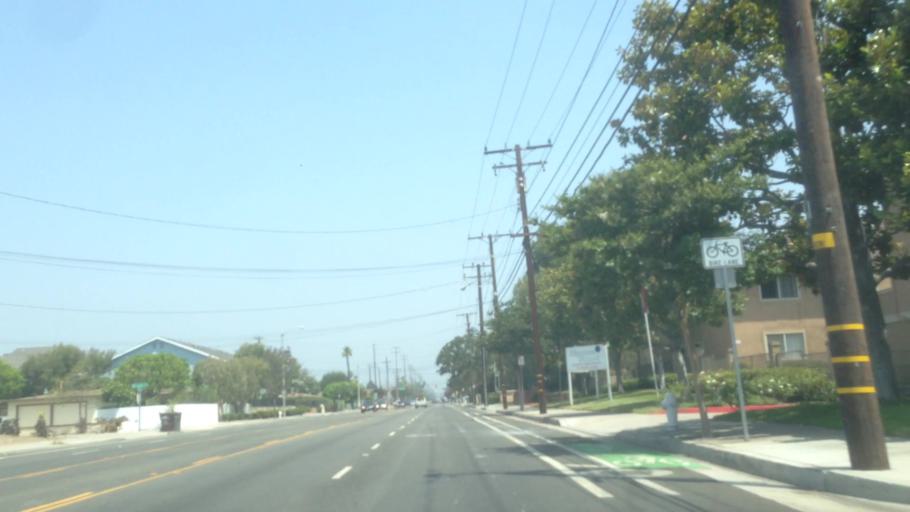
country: US
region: California
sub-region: Orange County
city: Garden Grove
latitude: 33.7420
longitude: -117.9287
